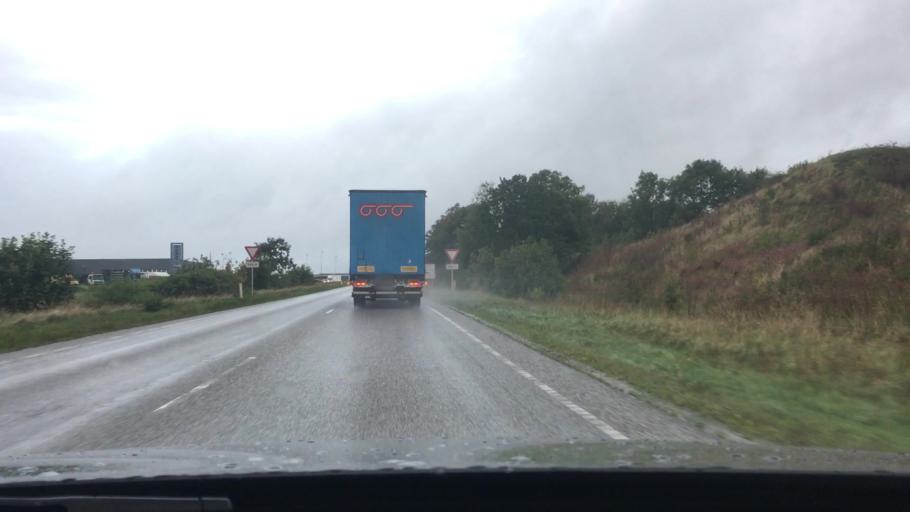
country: DK
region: Central Jutland
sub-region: Holstebro Kommune
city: Holstebro
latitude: 56.3327
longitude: 8.6529
